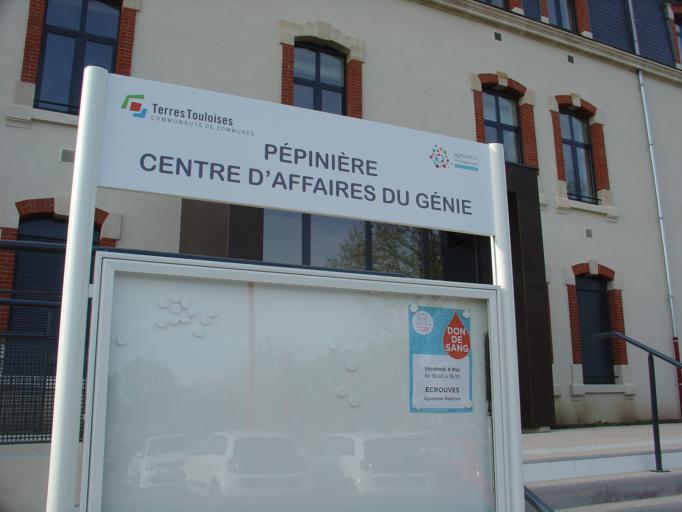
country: FR
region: Lorraine
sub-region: Departement de Meurthe-et-Moselle
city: Ecrouves
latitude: 48.6811
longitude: 5.8613
